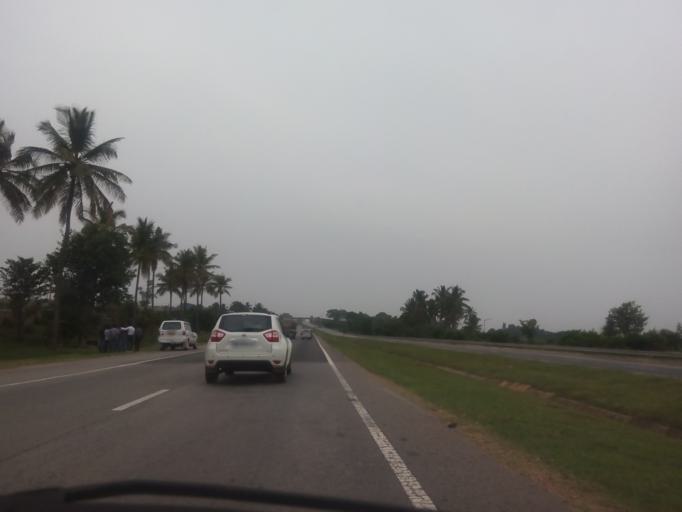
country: IN
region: Karnataka
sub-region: Bangalore Urban
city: Bangalore
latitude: 12.9342
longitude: 77.4695
